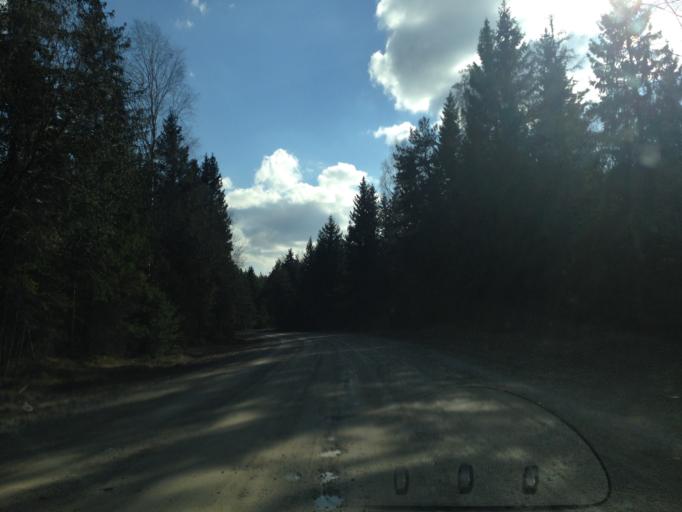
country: EE
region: Harju
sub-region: Nissi vald
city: Riisipere
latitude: 59.1194
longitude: 24.3539
